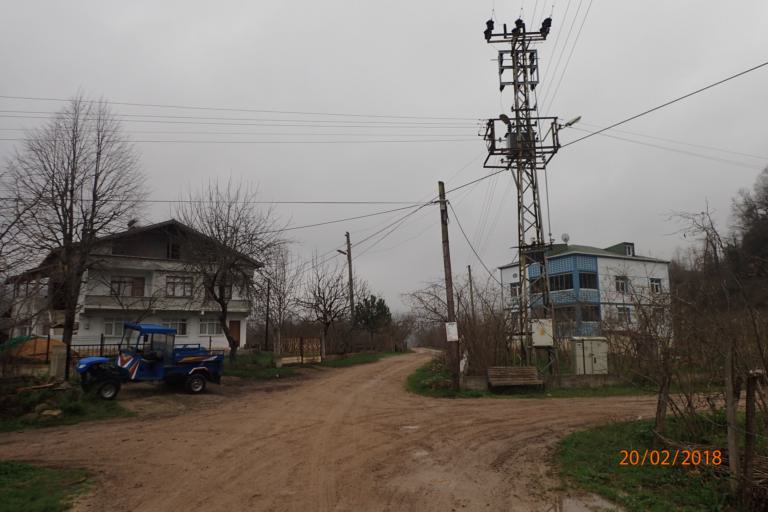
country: TR
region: Ordu
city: Camas
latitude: 40.9471
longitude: 37.5340
